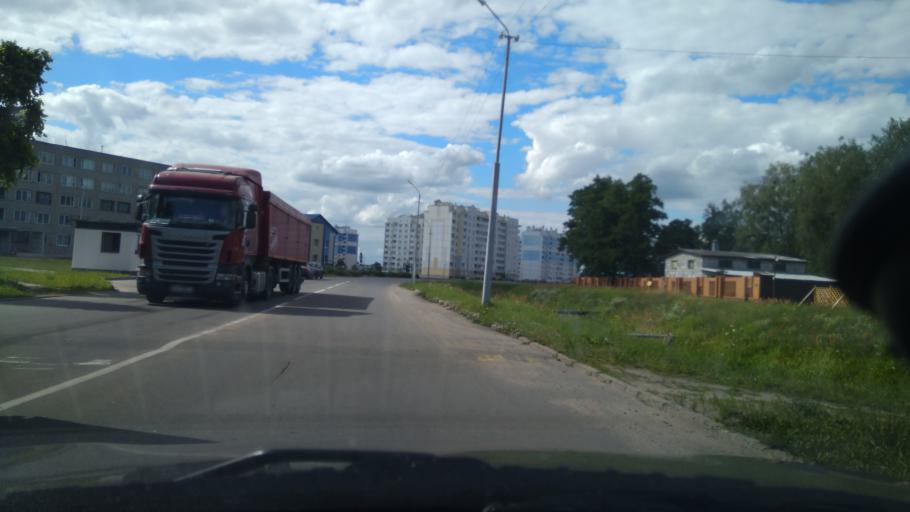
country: BY
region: Grodnenskaya
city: Masty
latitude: 53.4198
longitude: 24.5584
